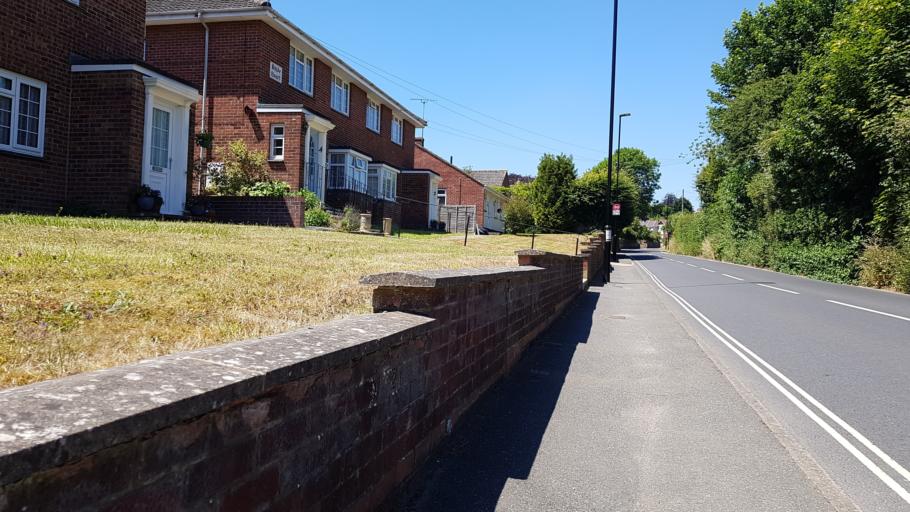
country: GB
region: England
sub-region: Isle of Wight
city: Newport
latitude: 50.6915
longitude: -1.2906
